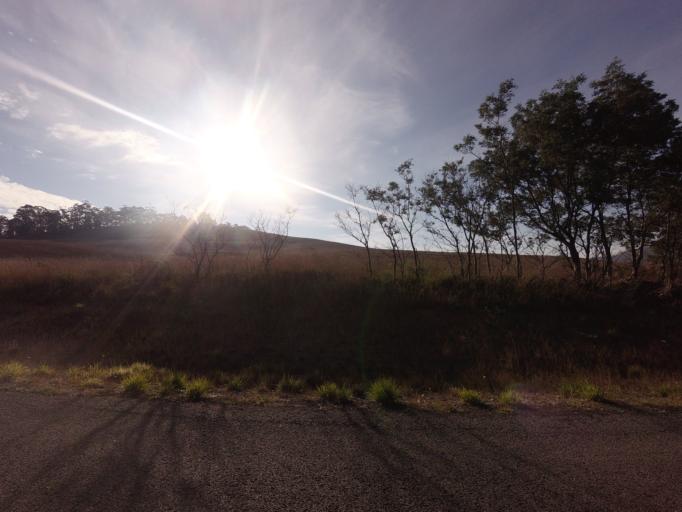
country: AU
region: Tasmania
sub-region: Brighton
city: Bridgewater
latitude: -42.5136
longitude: 147.3918
